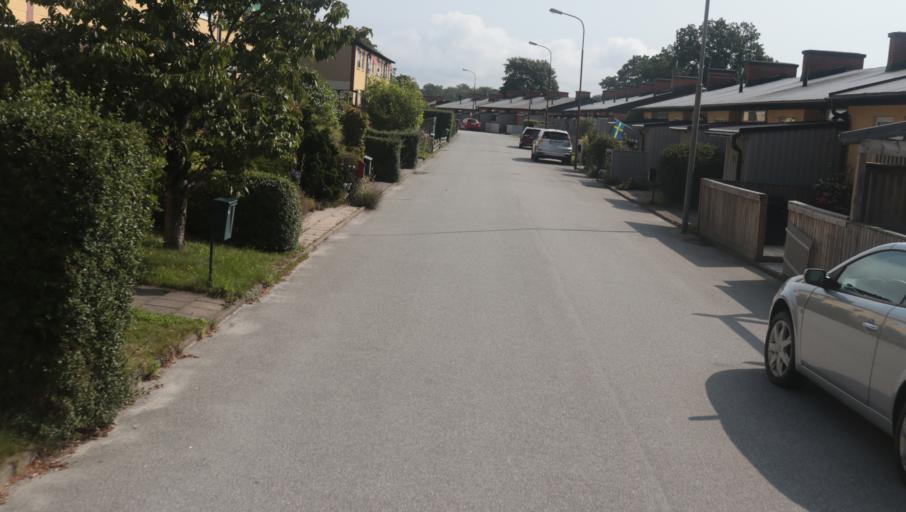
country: SE
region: Blekinge
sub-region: Karlshamns Kommun
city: Karlshamn
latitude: 56.1682
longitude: 14.8795
